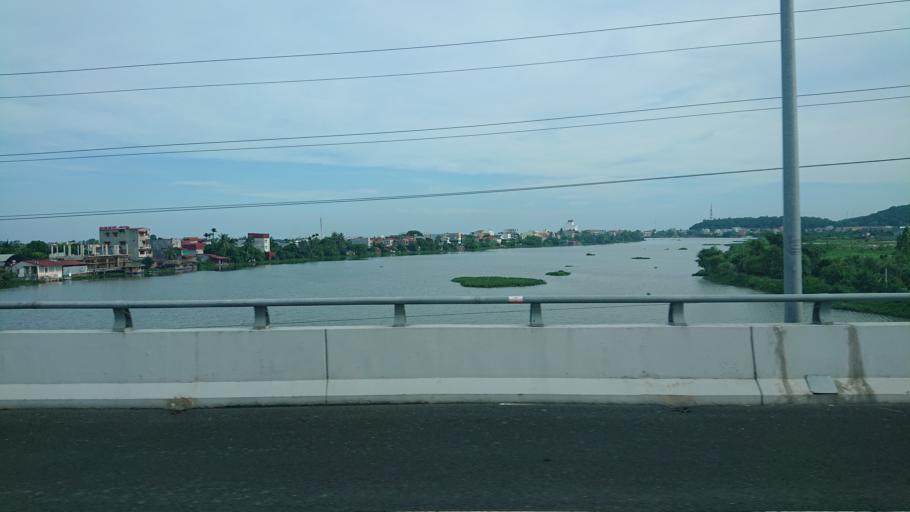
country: VN
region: Hai Phong
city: Nui Doi
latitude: 20.7653
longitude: 106.6750
